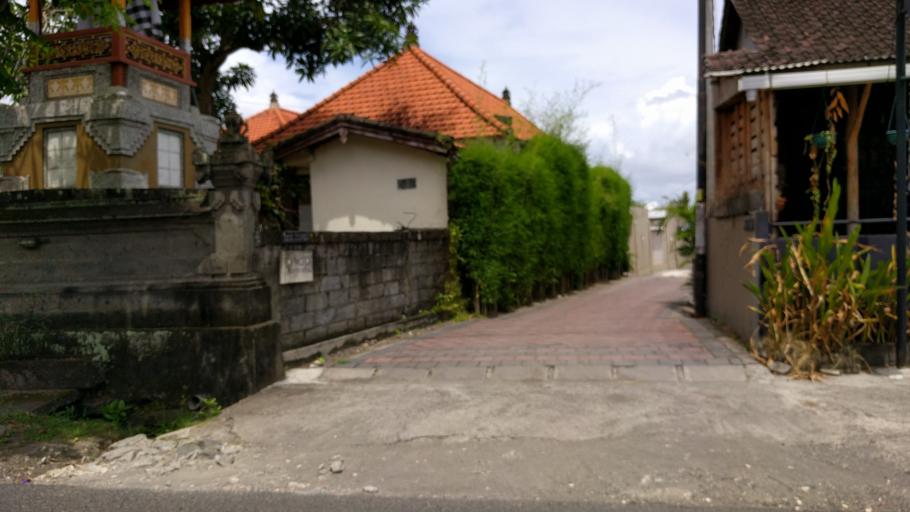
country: ID
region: Bali
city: Banjar Gunungpande
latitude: -8.6535
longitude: 115.1484
